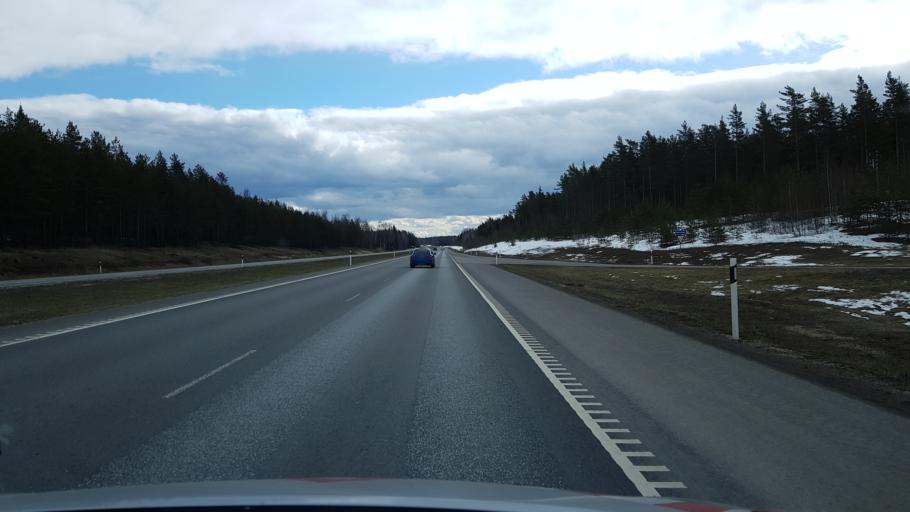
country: EE
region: Harju
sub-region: Loksa linn
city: Loksa
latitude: 59.4630
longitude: 25.7567
